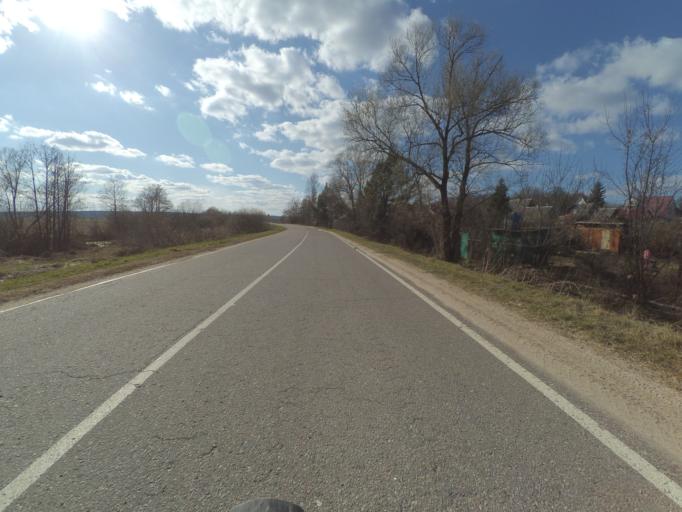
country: RU
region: Moskovskaya
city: Zhilevo
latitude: 54.8677
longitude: 37.8509
